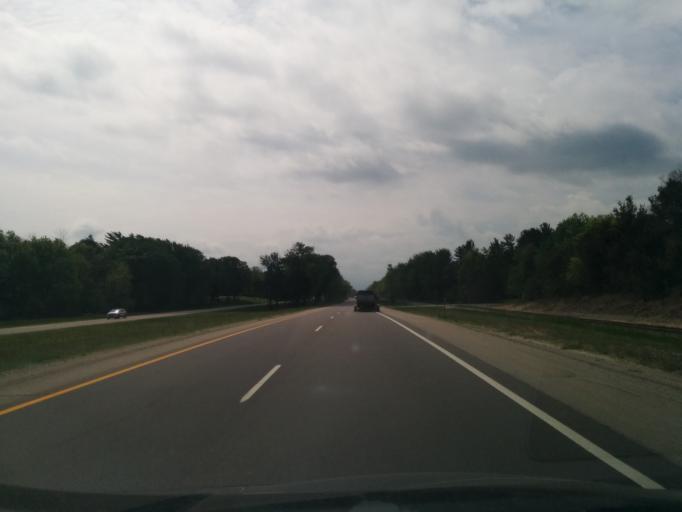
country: US
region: Michigan
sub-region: Ottawa County
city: Grand Haven
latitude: 42.9810
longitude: -86.1893
